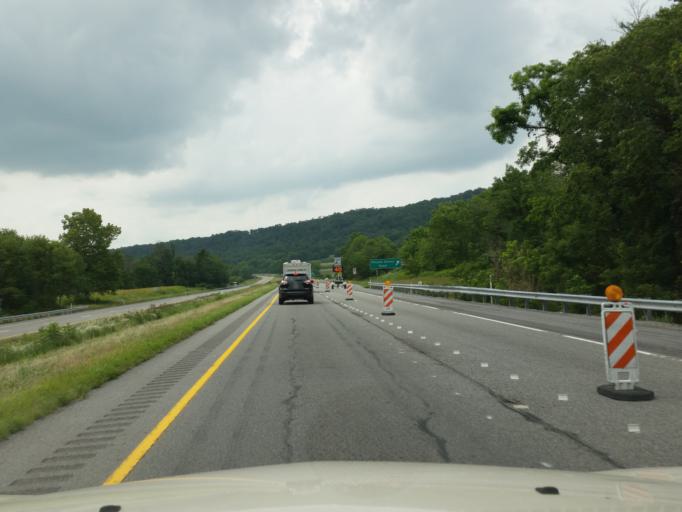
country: US
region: Pennsylvania
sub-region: Perry County
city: Newport
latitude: 40.5664
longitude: -77.1967
